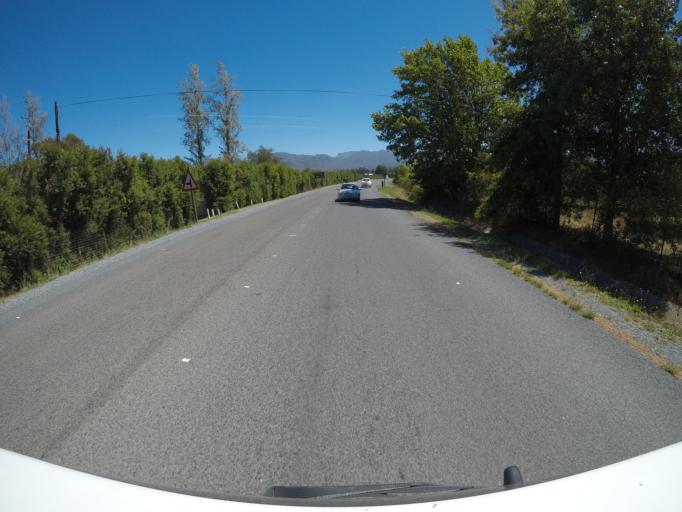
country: ZA
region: Western Cape
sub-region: Overberg District Municipality
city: Grabouw
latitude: -34.1765
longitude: 19.0345
